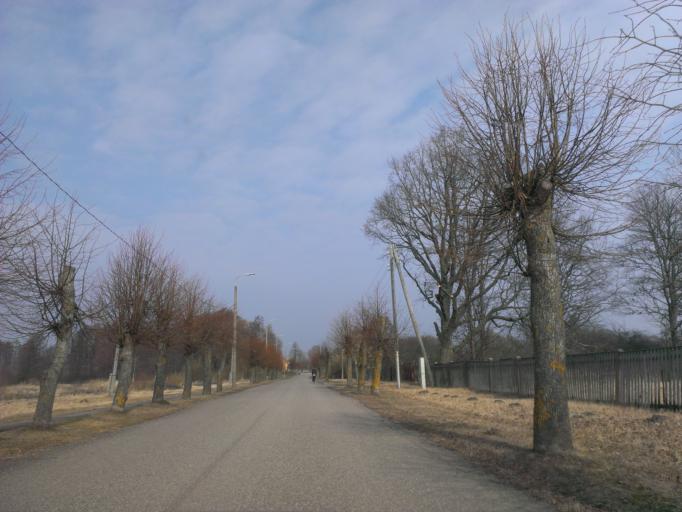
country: LV
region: Salacgrivas
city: Ainazi
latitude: 57.8708
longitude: 24.3607
